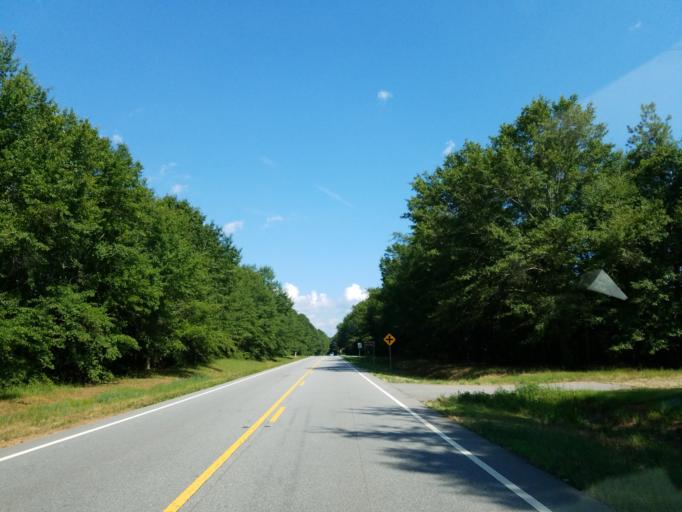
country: US
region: Georgia
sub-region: Lamar County
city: Barnesville
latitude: 32.9318
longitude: -84.0820
